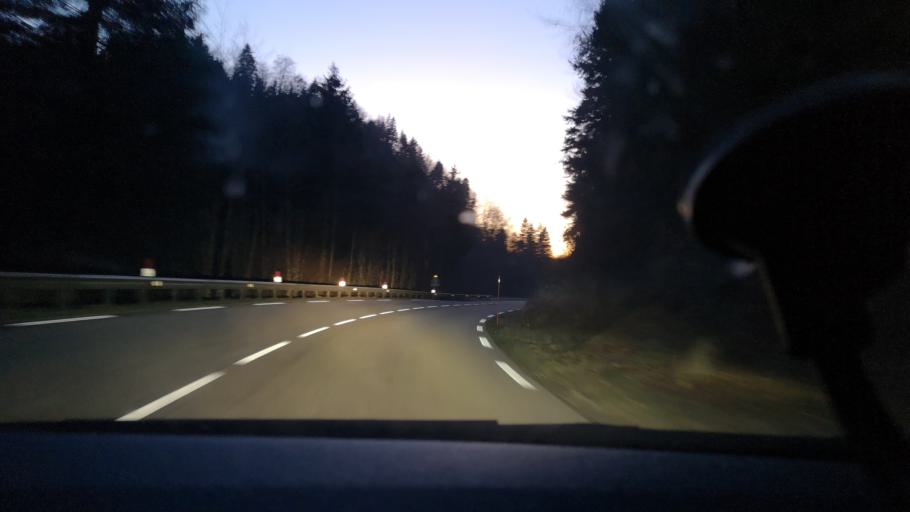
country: FR
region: Franche-Comte
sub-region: Departement du Jura
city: Champagnole
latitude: 46.7570
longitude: 5.9638
